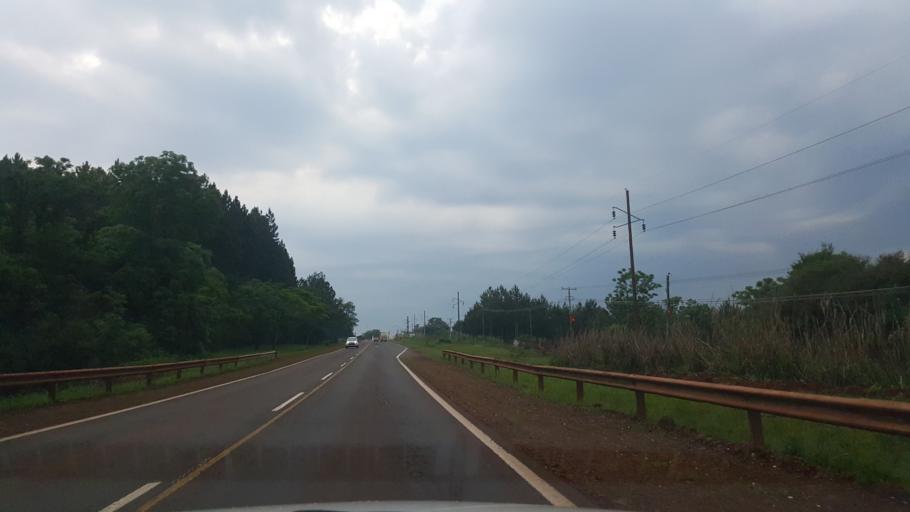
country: AR
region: Misiones
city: Capiovi
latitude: -26.9366
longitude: -55.0691
